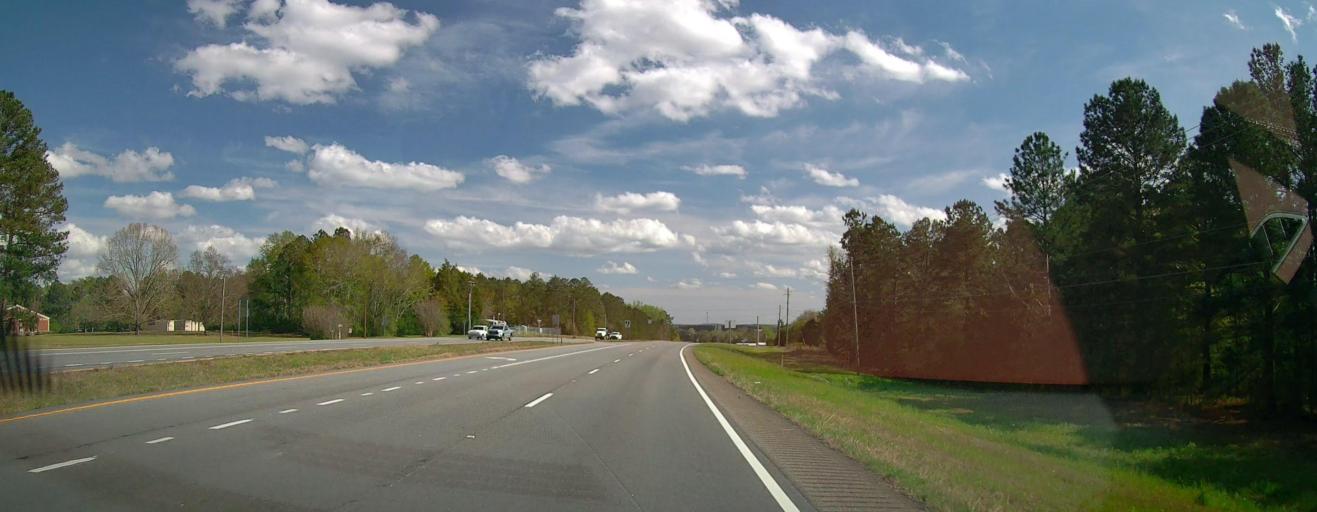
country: US
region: Georgia
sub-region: Baldwin County
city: Hardwick
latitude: 33.0182
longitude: -83.2282
